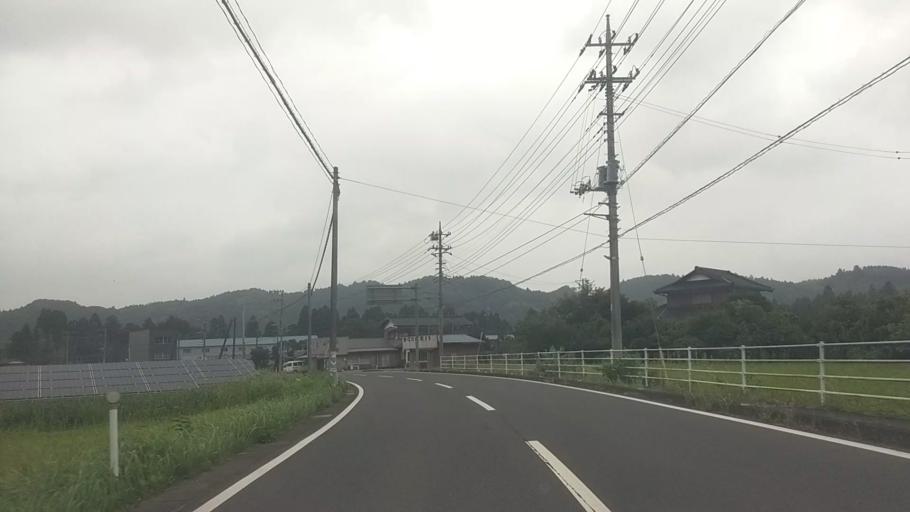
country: JP
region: Chiba
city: Ohara
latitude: 35.2640
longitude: 140.2544
